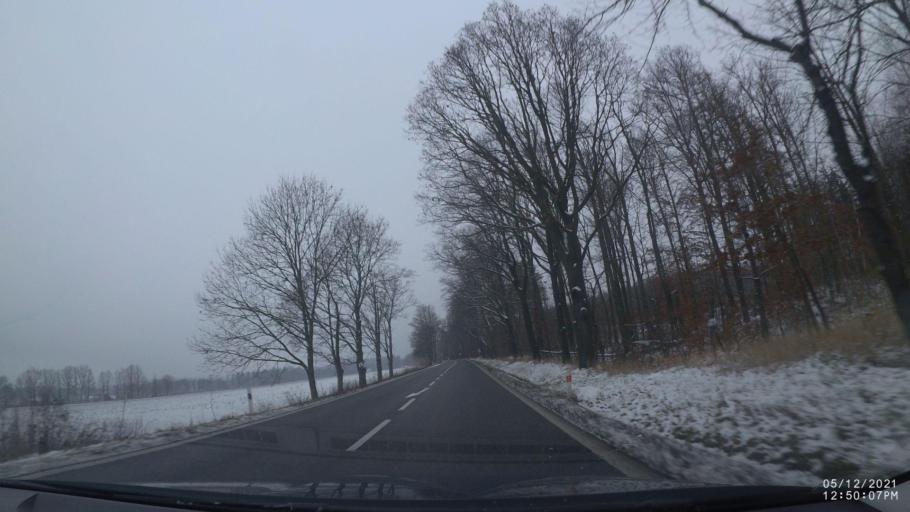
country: CZ
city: Nove Mesto nad Metuji
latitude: 50.3820
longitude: 16.1439
